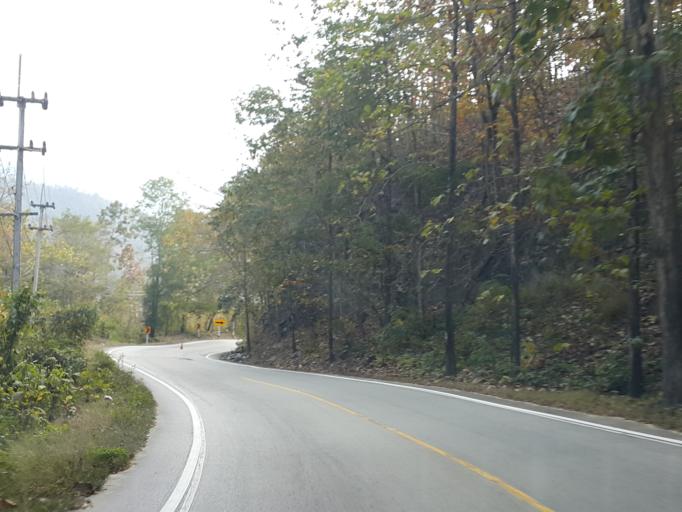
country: TH
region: Chiang Mai
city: Hot
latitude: 18.2024
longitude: 98.4493
